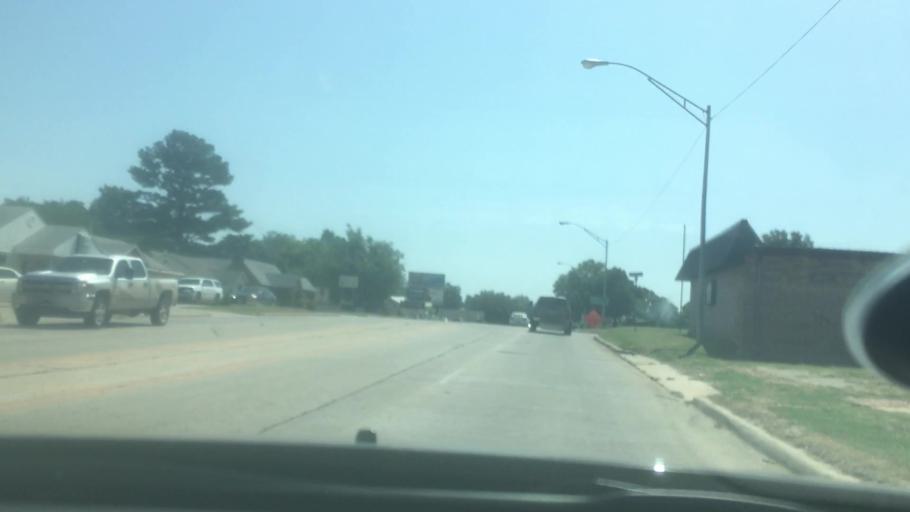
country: US
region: Oklahoma
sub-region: Pontotoc County
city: Ada
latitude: 34.7816
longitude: -96.6684
